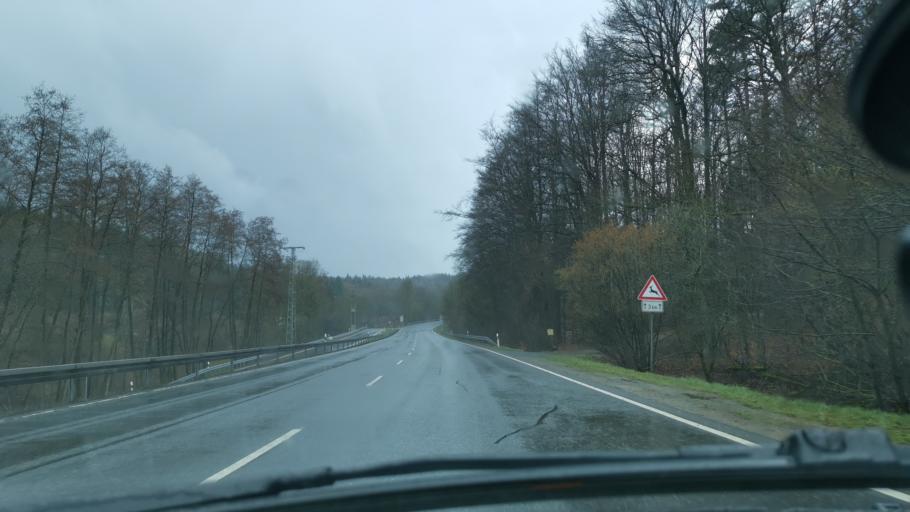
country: DE
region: Hesse
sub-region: Regierungsbezirk Kassel
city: Cornberg
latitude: 51.0340
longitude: 9.8583
